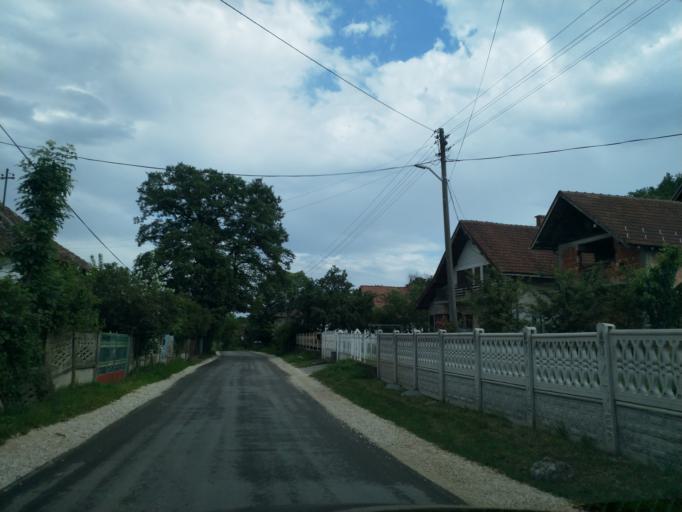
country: RS
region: Central Serbia
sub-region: Borski Okrug
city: Bor
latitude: 44.0156
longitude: 21.9824
